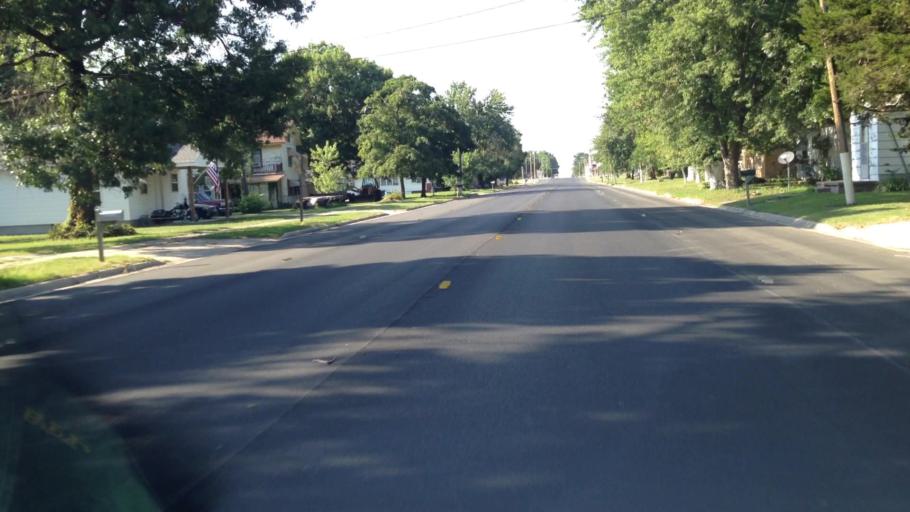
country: US
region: Kansas
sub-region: Allen County
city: Iola
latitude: 37.9113
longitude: -95.1701
